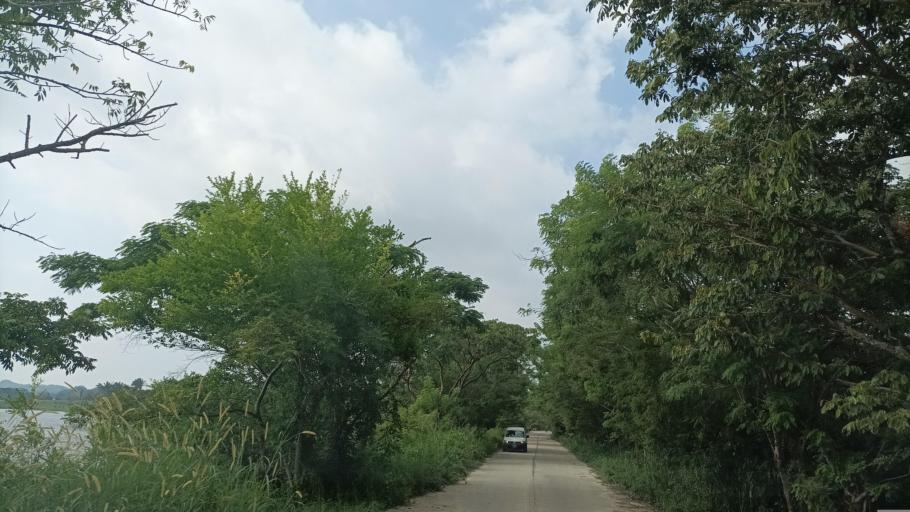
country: MX
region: Veracruz
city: Villa Nanchital
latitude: 18.0931
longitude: -94.2920
